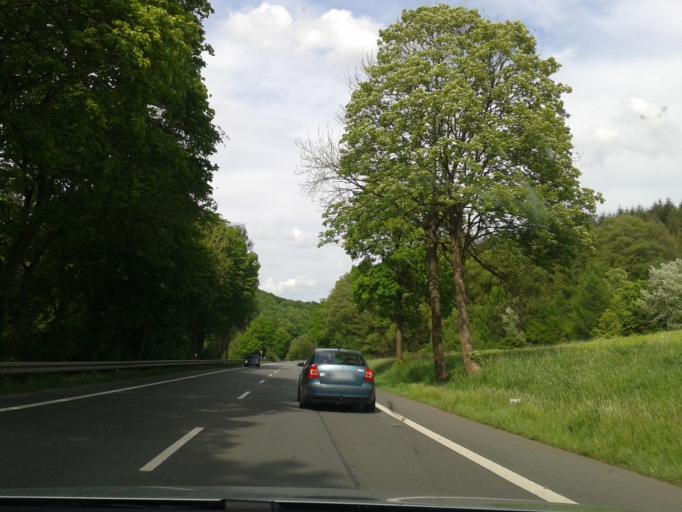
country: DE
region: Hesse
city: Frankenberg
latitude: 51.1119
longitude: 8.8536
